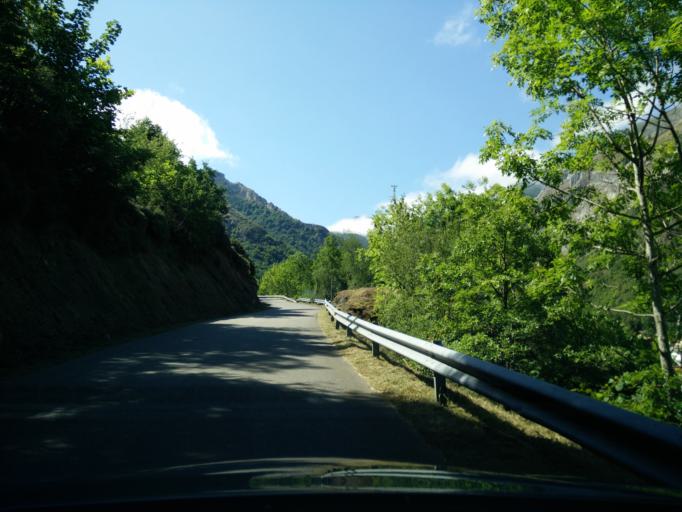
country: ES
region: Asturias
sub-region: Province of Asturias
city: Pola de Somiedo
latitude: 43.0970
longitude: -6.2547
